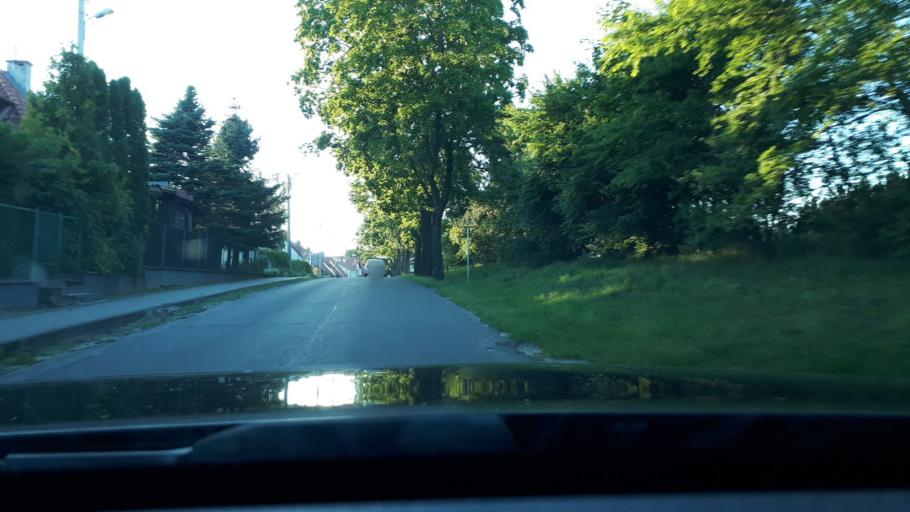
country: PL
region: Warmian-Masurian Voivodeship
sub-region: Powiat olsztynski
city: Stawiguda
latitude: 53.6548
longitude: 20.4026
